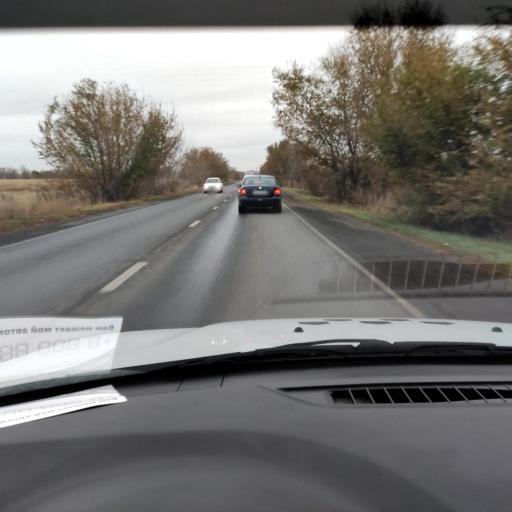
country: RU
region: Samara
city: Podstepki
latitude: 53.5186
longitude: 49.2283
